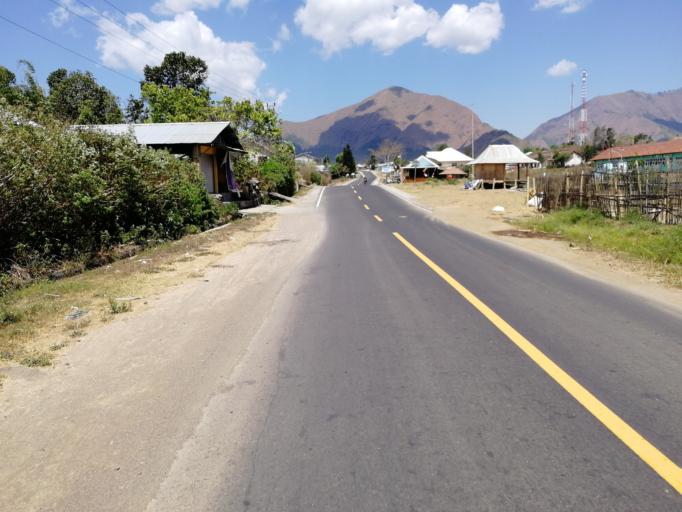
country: ID
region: West Nusa Tenggara
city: Sembalunlawang
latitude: -8.3578
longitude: 116.5192
